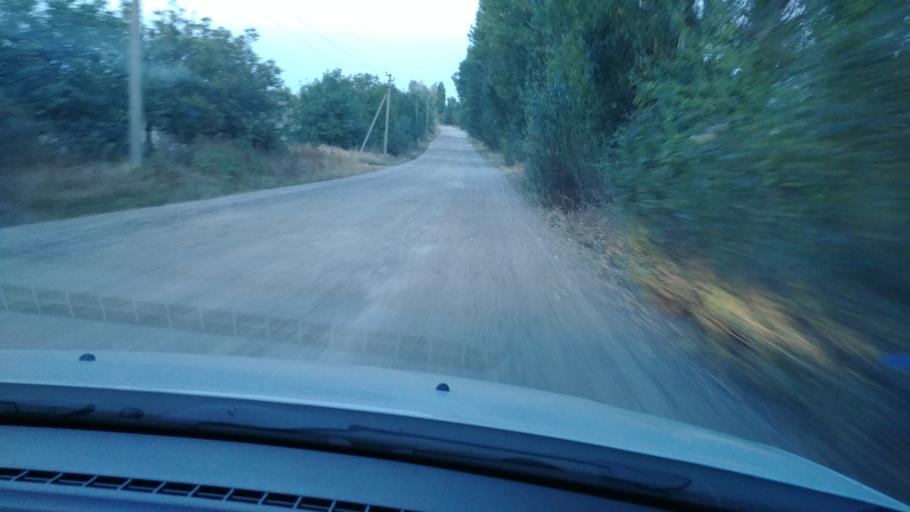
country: MD
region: Rezina
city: Saharna
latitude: 47.6780
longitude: 28.9235
